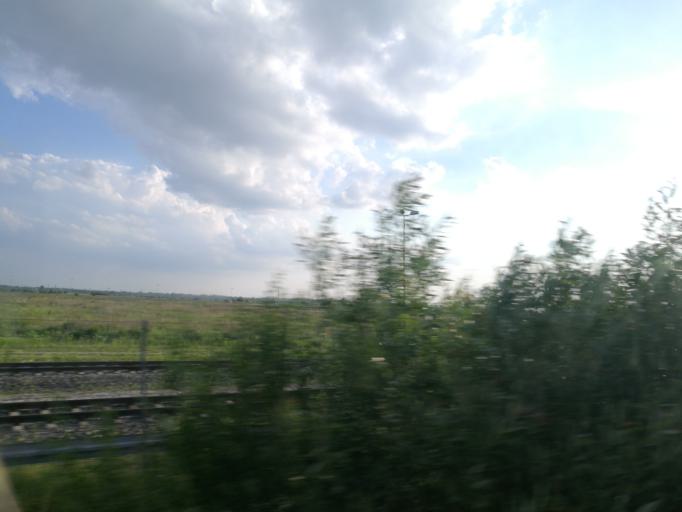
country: RO
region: Arges
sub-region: Comuna Leordeni
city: Leordeni
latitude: 44.7863
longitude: 25.1161
